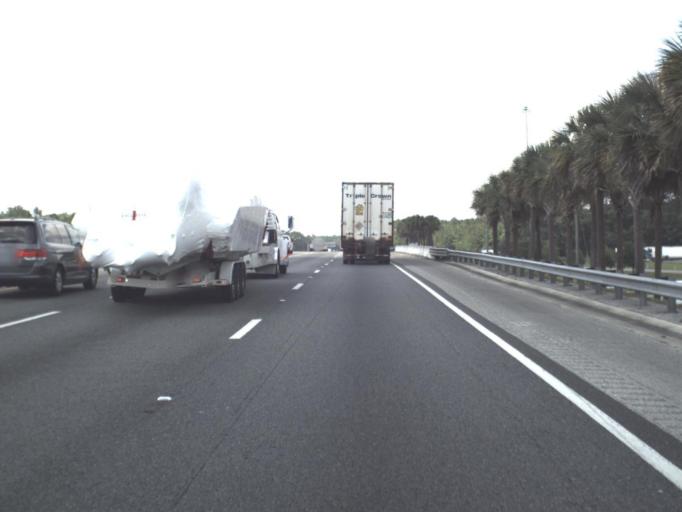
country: US
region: Florida
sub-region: Saint Johns County
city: Fruit Cove
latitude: 30.0641
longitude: -81.4980
